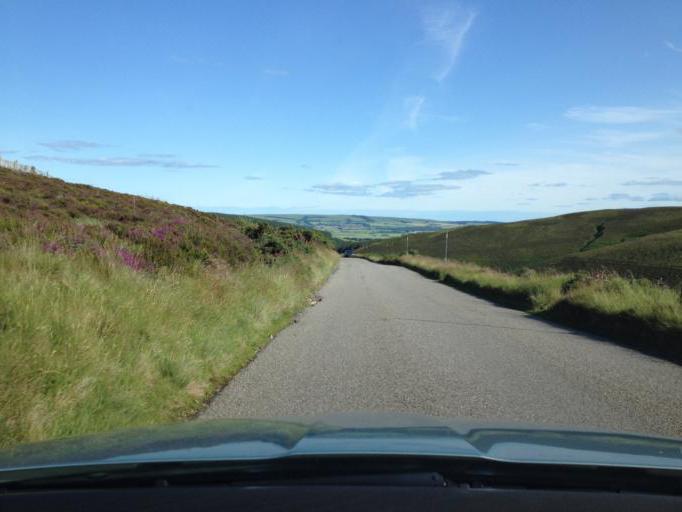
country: GB
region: Scotland
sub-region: Aberdeenshire
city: Laurencekirk
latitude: 56.9033
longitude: -2.5698
